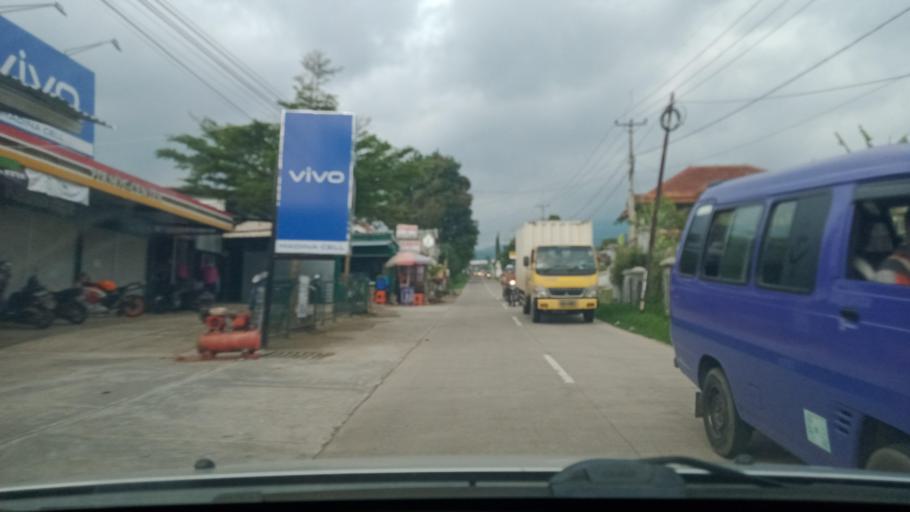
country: ID
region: West Java
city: Lembang
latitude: -6.8099
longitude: 107.5772
